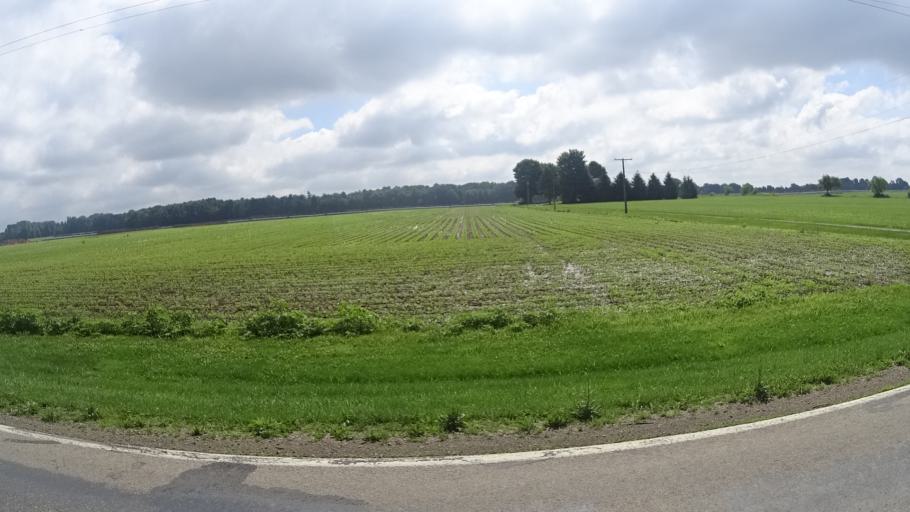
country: US
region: Ohio
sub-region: Huron County
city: Wakeman
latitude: 41.2922
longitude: -82.4130
